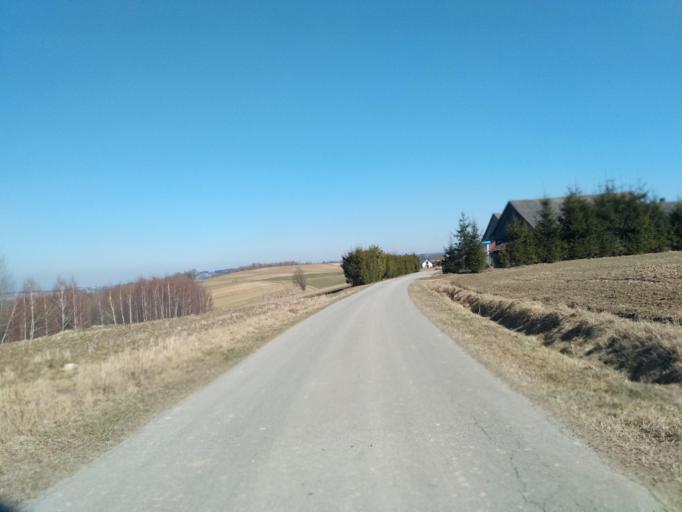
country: PL
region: Subcarpathian Voivodeship
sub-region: Powiat ropczycko-sedziszowski
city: Niedzwiada
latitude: 49.9543
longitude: 21.5408
